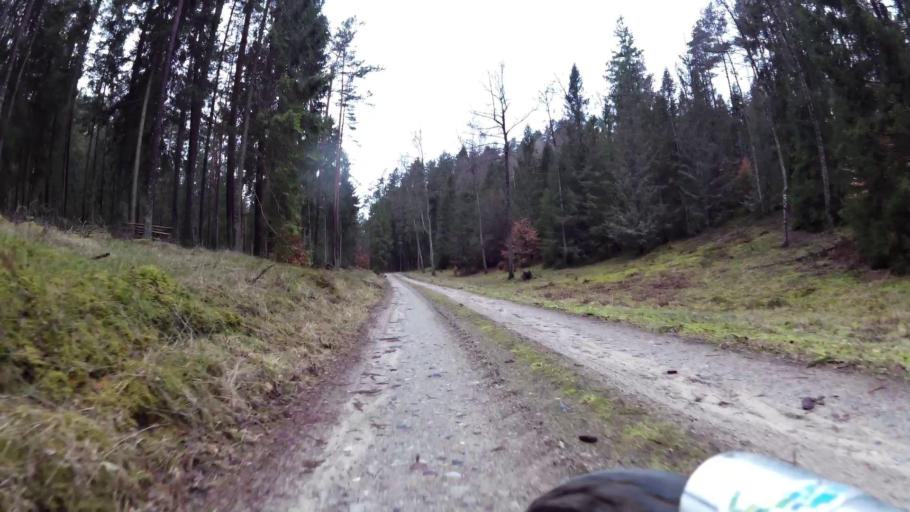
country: PL
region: Pomeranian Voivodeship
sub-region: Powiat bytowski
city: Borzytuchom
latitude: 54.2572
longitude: 17.3182
